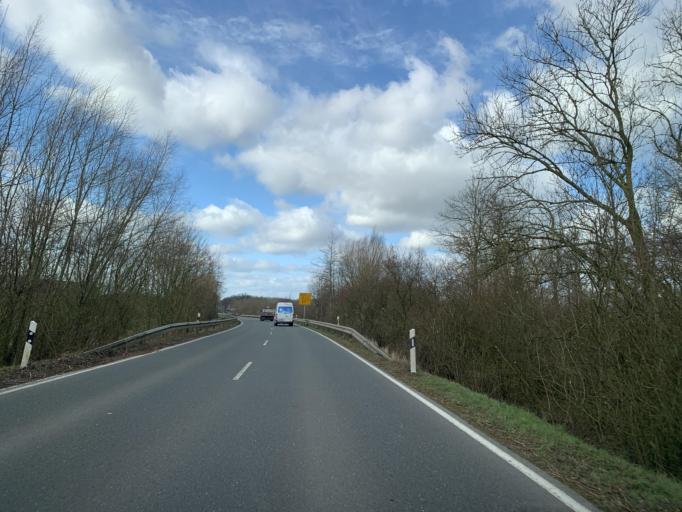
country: DE
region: North Rhine-Westphalia
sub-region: Regierungsbezirk Munster
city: Billerbeck
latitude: 52.0302
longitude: 7.2772
